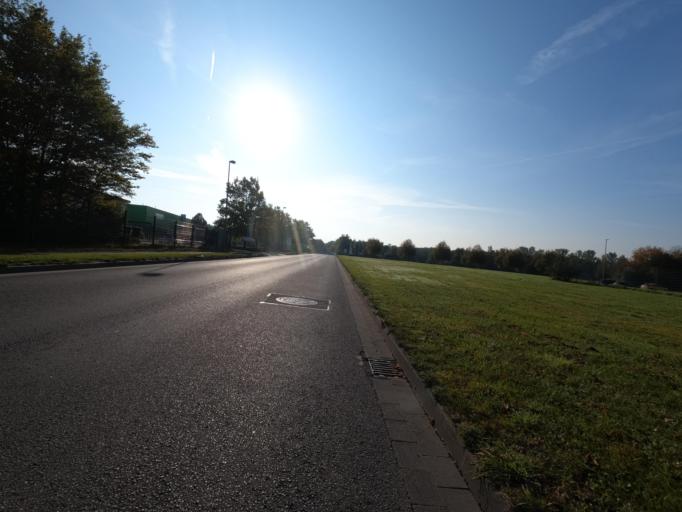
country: DE
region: North Rhine-Westphalia
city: Huckelhoven
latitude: 51.0328
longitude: 6.2585
